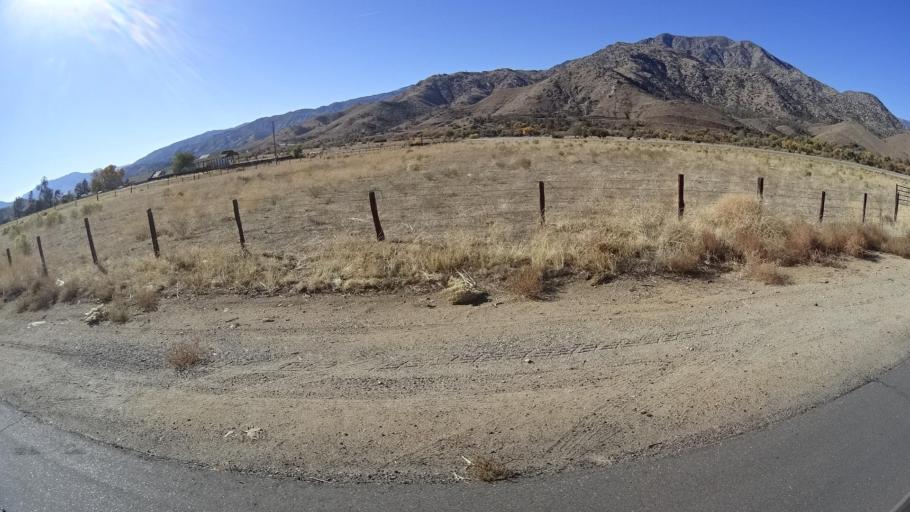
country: US
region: California
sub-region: Kern County
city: Kernville
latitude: 35.7297
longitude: -118.4164
